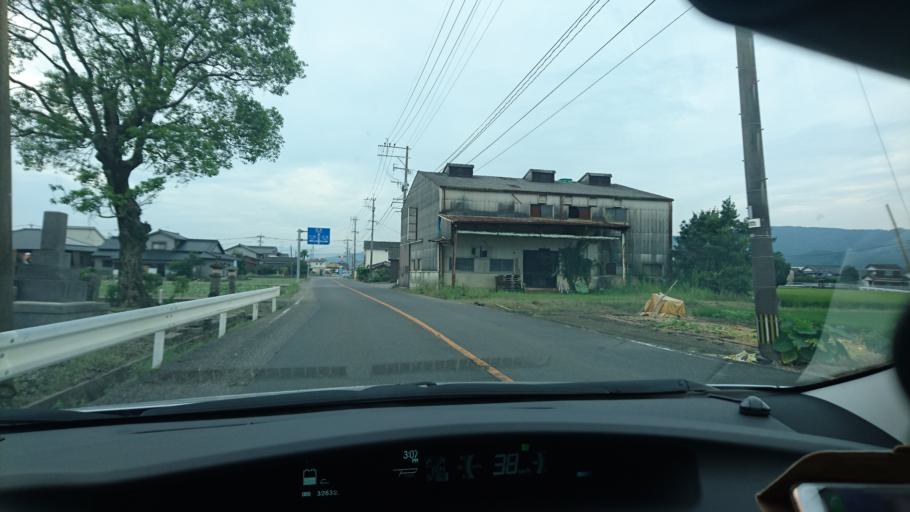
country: JP
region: Saga Prefecture
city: Kashima
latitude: 33.1961
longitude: 130.1145
